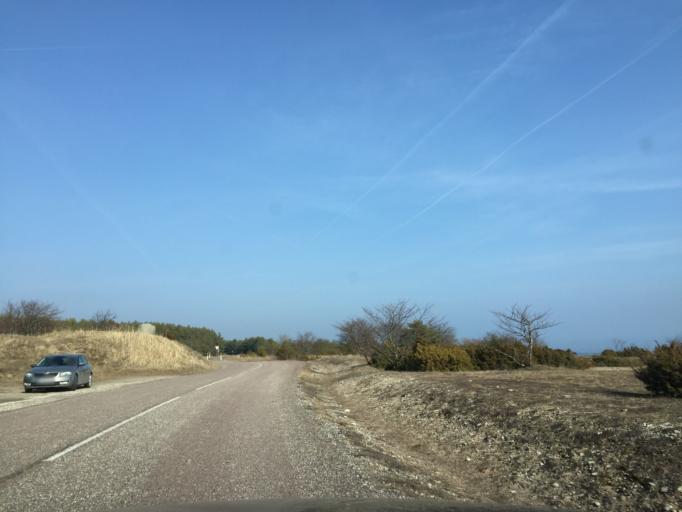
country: LV
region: Dundaga
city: Dundaga
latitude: 57.9172
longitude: 22.0631
